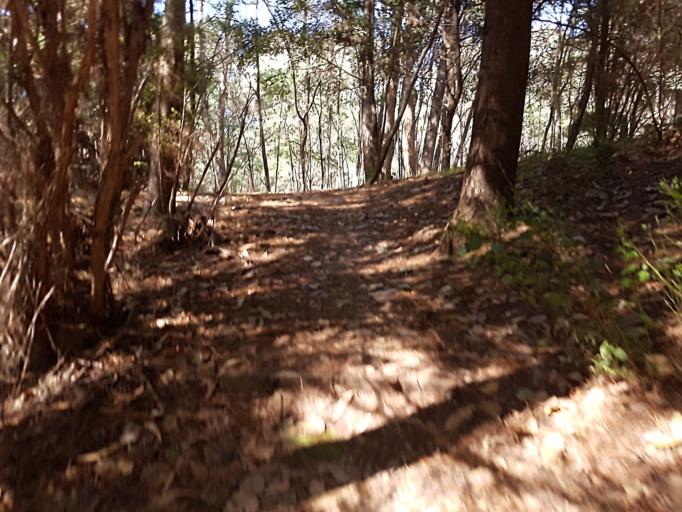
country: AU
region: Victoria
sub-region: Alpine
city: Mount Beauty
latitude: -36.8972
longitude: 147.0690
